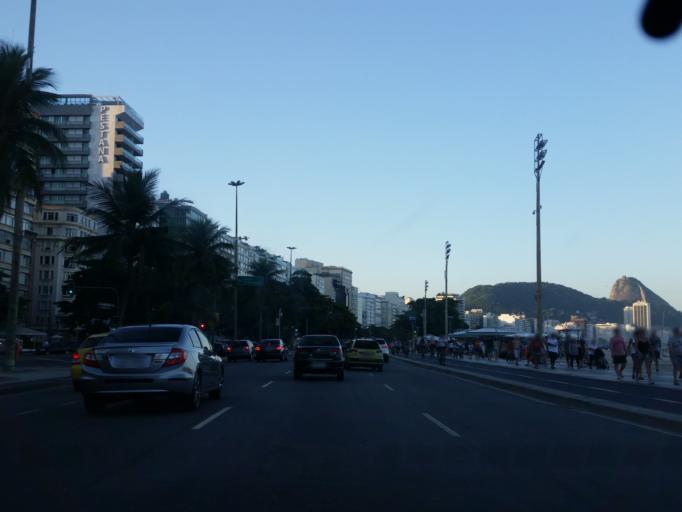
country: BR
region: Rio de Janeiro
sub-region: Rio De Janeiro
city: Rio de Janeiro
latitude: -22.9768
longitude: -43.1881
